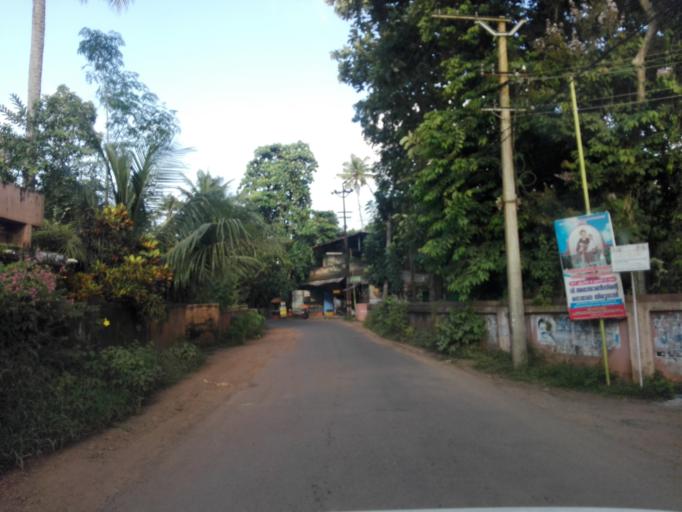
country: IN
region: Kerala
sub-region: Kottayam
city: Kottayam
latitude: 9.6105
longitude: 76.4951
